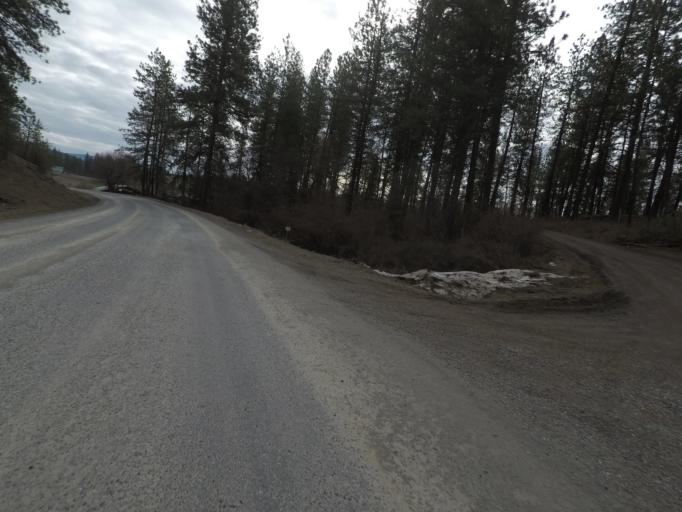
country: US
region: Washington
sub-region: Stevens County
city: Colville
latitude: 48.4975
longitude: -117.8369
